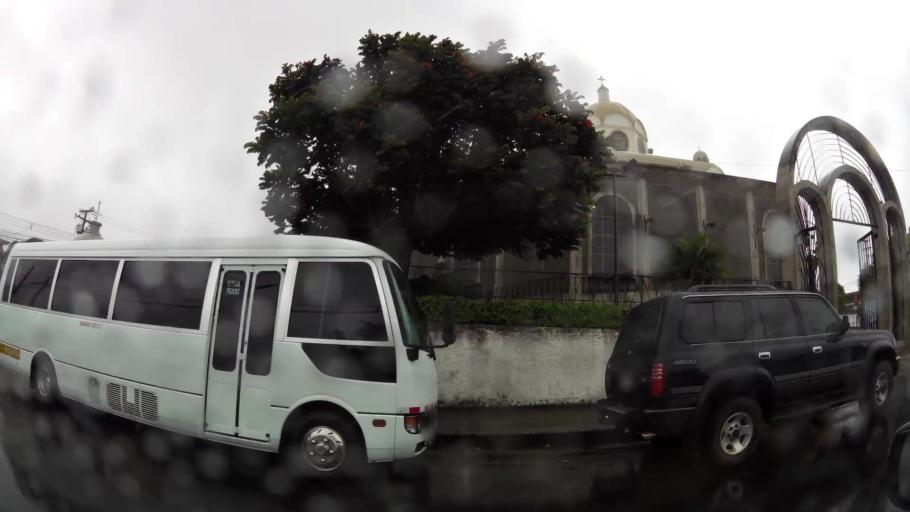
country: CR
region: Cartago
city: Cartago
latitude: 9.8640
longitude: -83.9124
